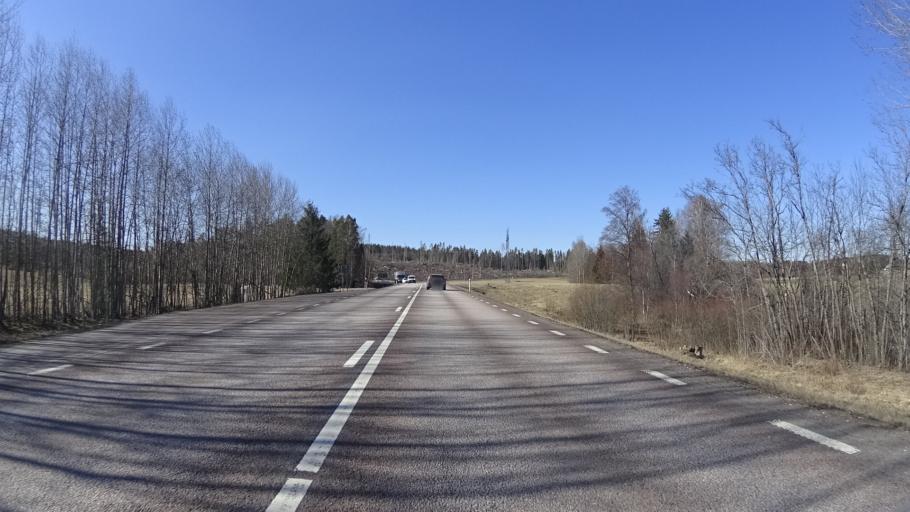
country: SE
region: Vaermland
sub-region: Karlstads Kommun
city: Edsvalla
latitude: 59.5216
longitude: 13.1591
